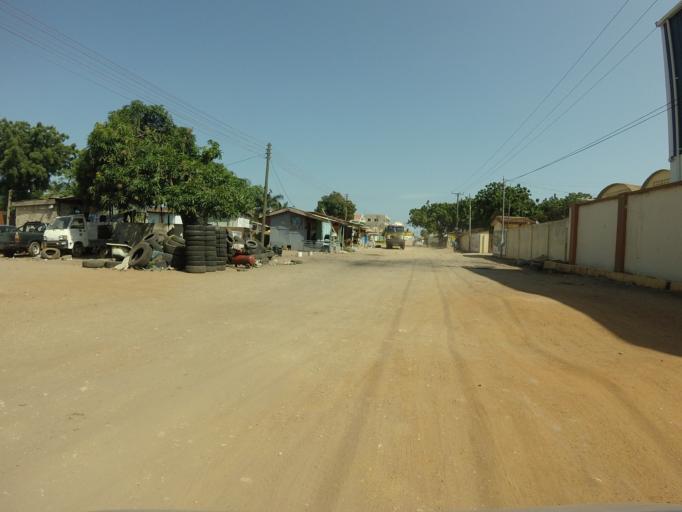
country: GH
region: Greater Accra
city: Dome
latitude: 5.6371
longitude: -0.2340
